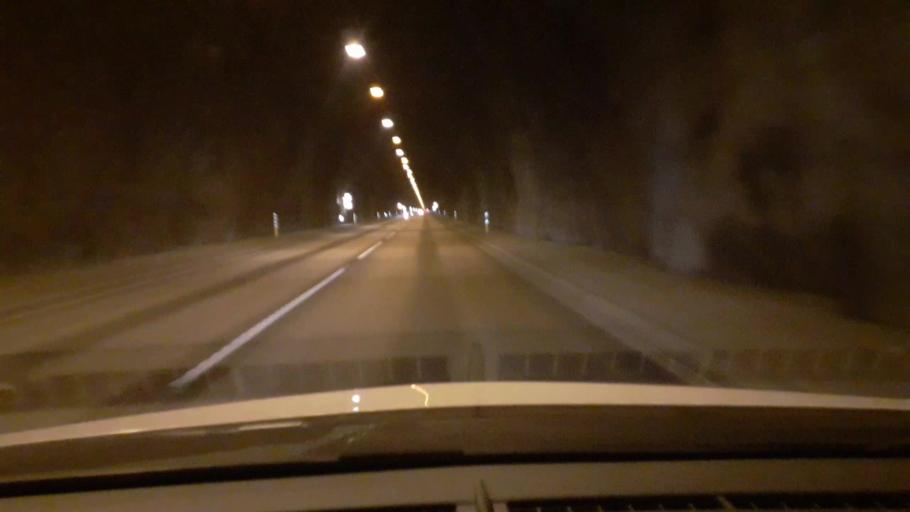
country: IS
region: Capital Region
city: Reykjavik
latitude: 64.2977
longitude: -21.8753
